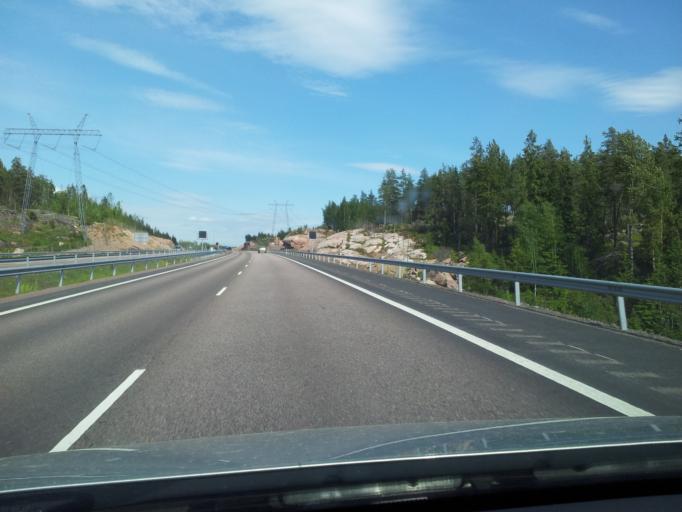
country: FI
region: Uusimaa
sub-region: Loviisa
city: Ruotsinpyhtaeae
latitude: 60.4882
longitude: 26.3989
